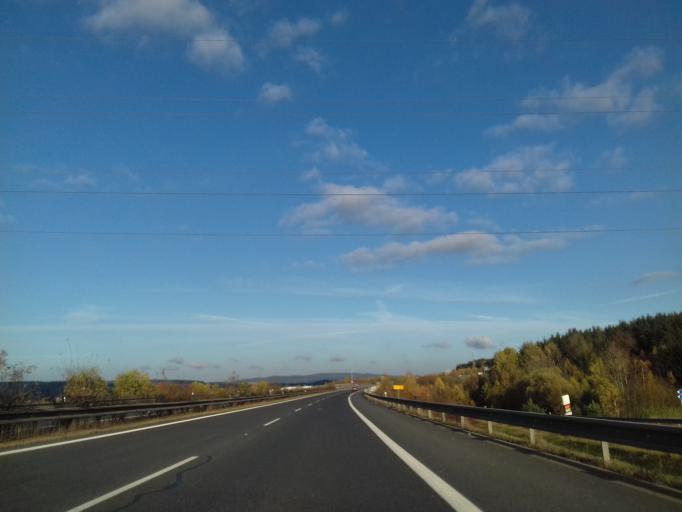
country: CZ
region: Plzensky
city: Dysina
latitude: 49.7336
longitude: 13.5047
